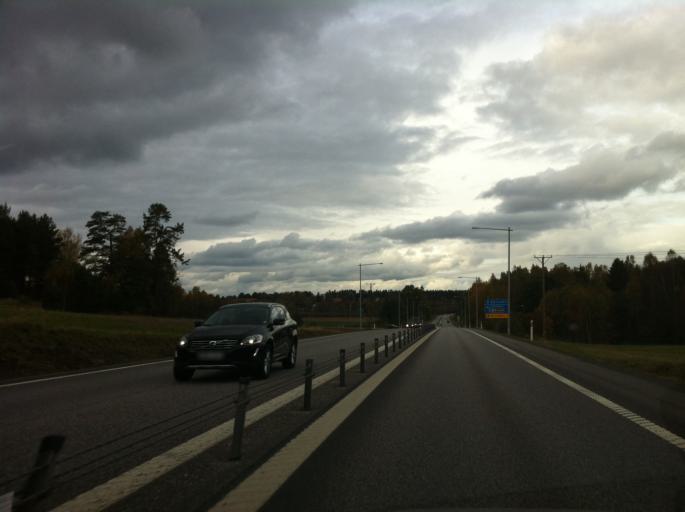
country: SE
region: OEstergoetland
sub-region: Motala Kommun
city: Motala
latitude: 58.6047
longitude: 14.9859
